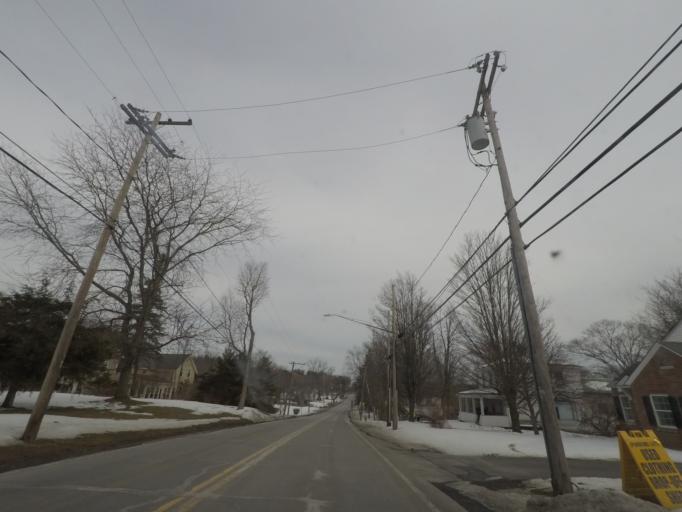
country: US
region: New York
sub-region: Albany County
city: Voorheesville
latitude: 42.5754
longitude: -73.9577
